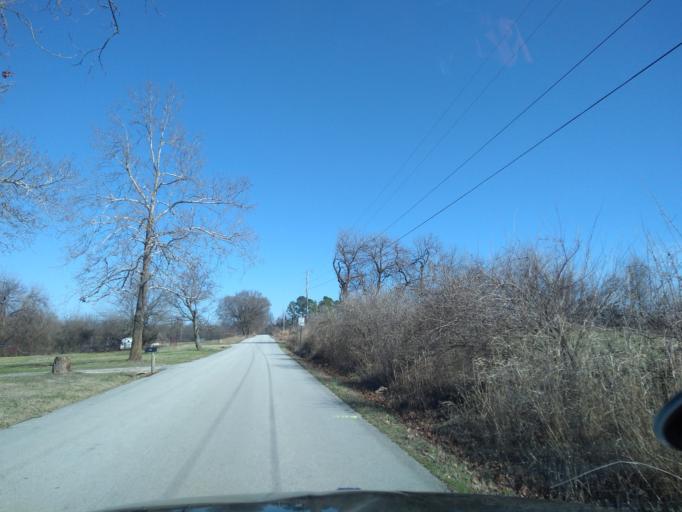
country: US
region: Arkansas
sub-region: Washington County
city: Farmington
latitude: 36.0610
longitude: -94.2456
